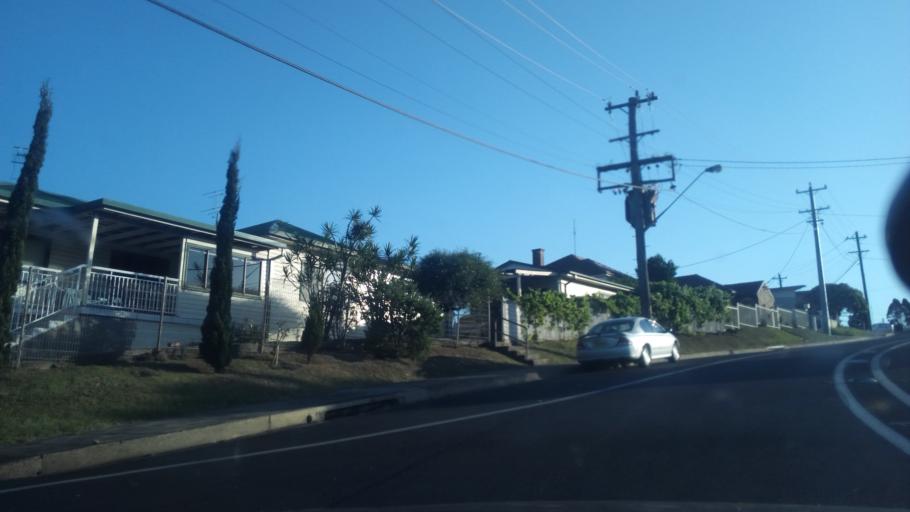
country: AU
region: New South Wales
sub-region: Wollongong
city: Lake Heights
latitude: -34.4775
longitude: 150.8724
